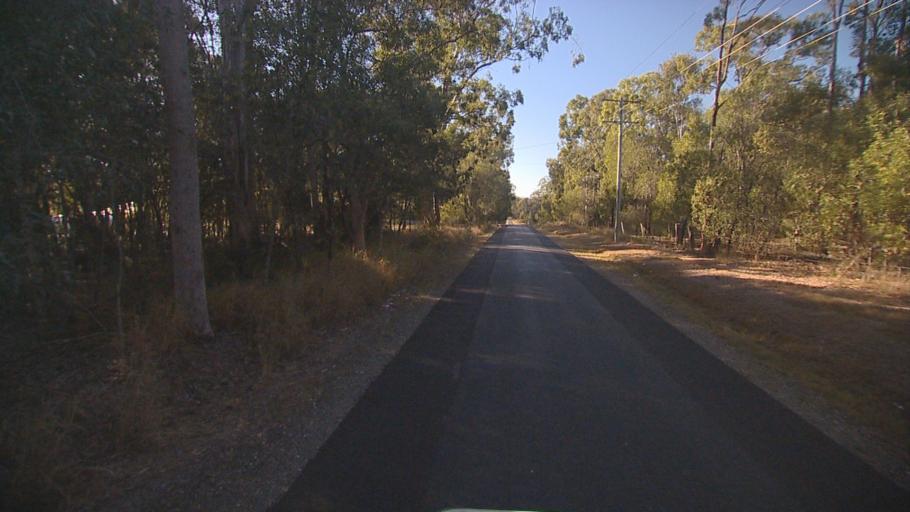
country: AU
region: Queensland
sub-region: Logan
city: North Maclean
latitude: -27.7905
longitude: 152.9854
